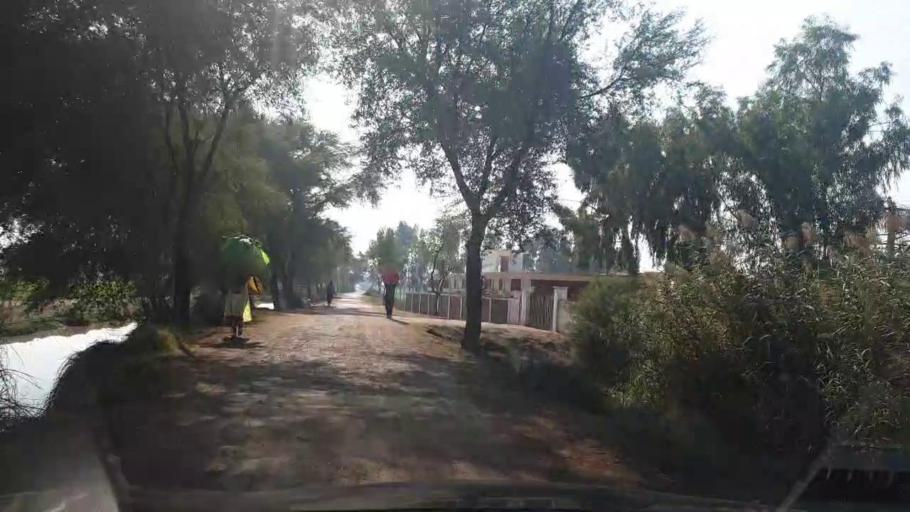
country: PK
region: Sindh
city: Khairpur
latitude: 28.1338
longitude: 69.6478
